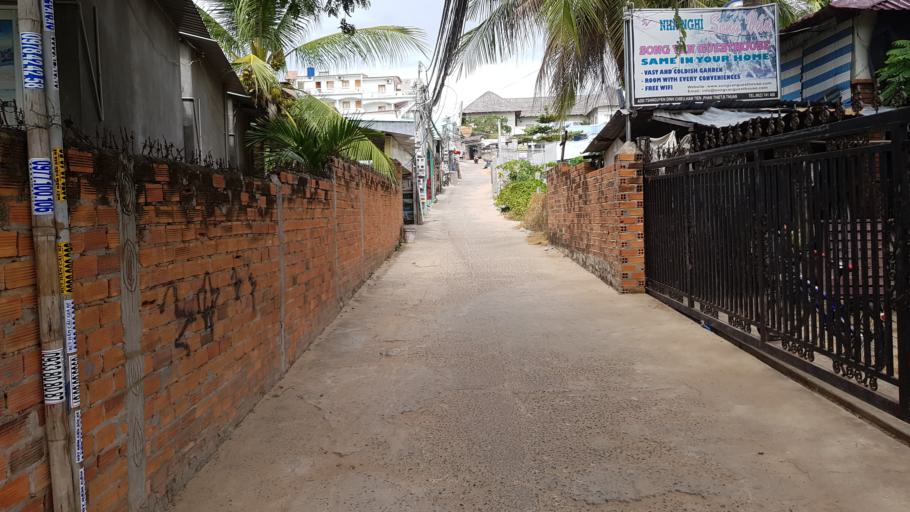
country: VN
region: Binh Thuan
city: Phan Thiet
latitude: 10.9482
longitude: 108.2001
